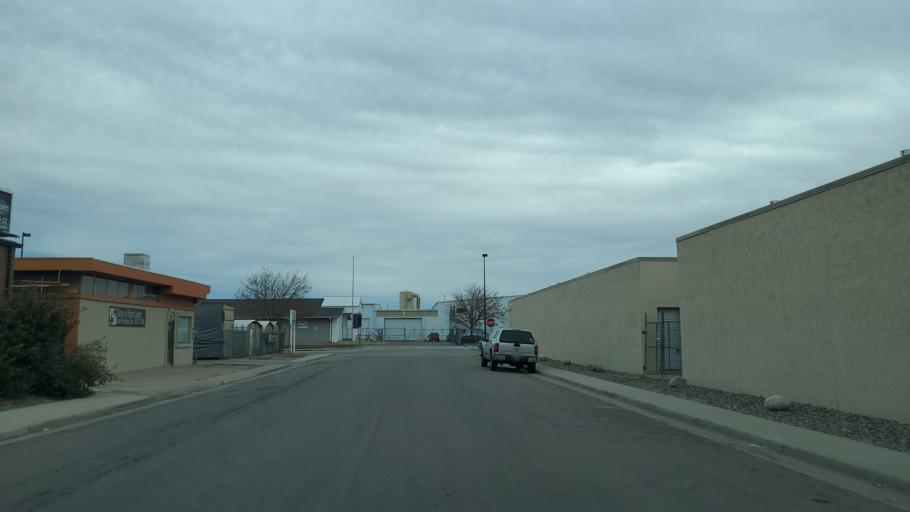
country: US
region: Colorado
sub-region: Denver County
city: Denver
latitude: 39.6960
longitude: -104.9980
